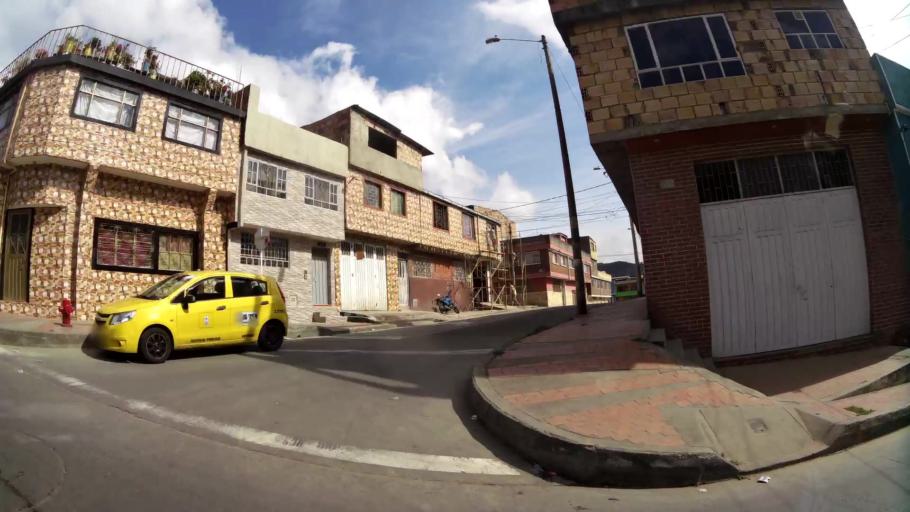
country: CO
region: Bogota D.C.
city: Bogota
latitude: 4.5519
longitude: -74.0964
